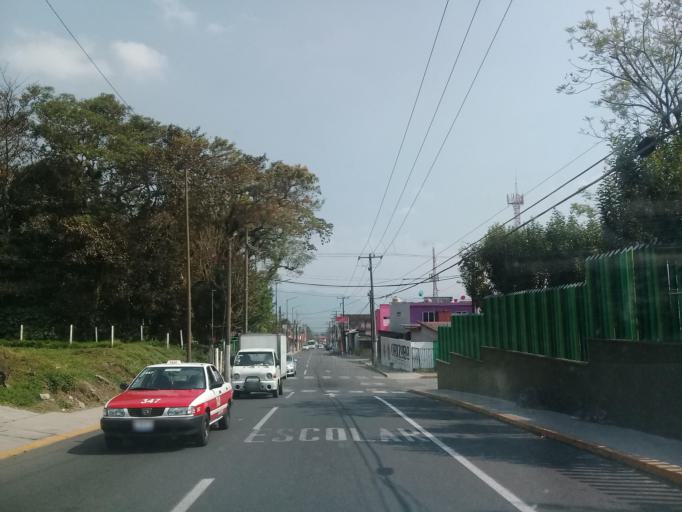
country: MX
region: Veracruz
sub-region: Mariano Escobedo
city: Palmira
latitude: 18.8749
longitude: -97.1054
